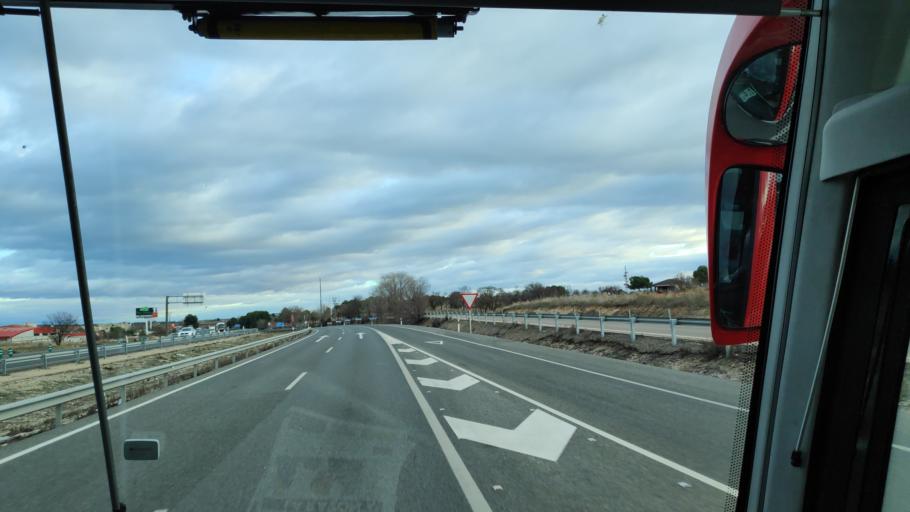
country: ES
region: Madrid
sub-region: Provincia de Madrid
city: Villarejo de Salvanes
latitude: 40.1702
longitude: -3.2905
